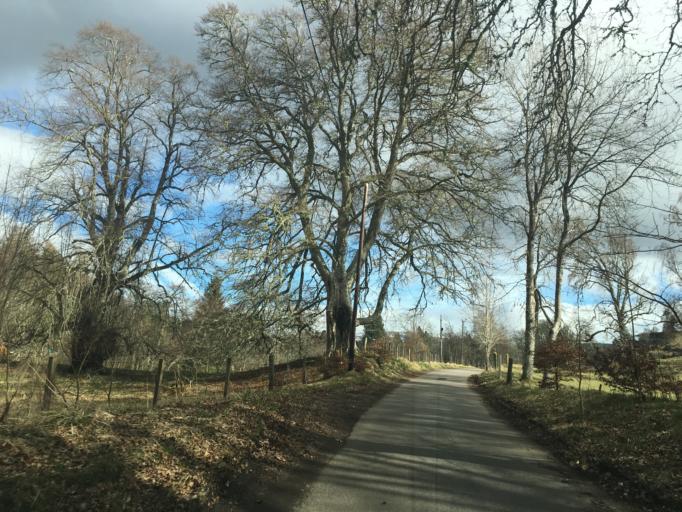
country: GB
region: Scotland
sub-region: Highland
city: Aviemore
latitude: 57.1641
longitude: -3.8346
